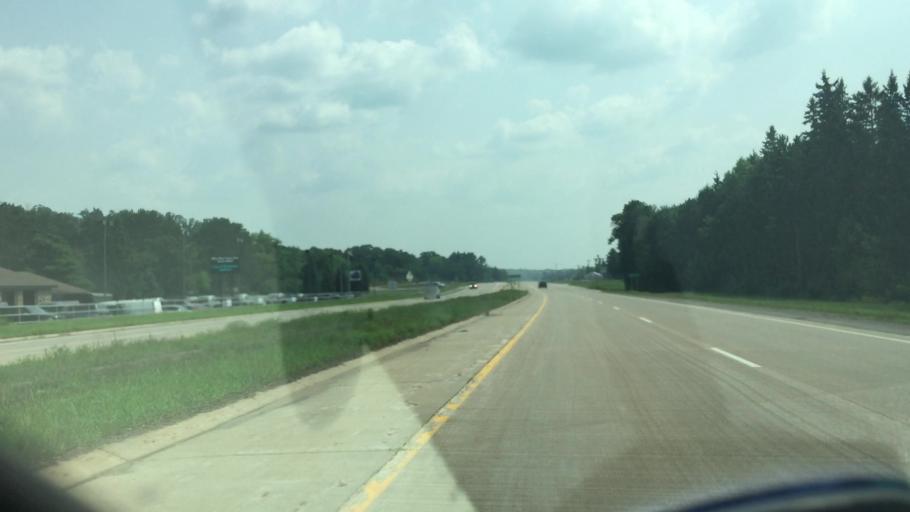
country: US
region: Wisconsin
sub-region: Eau Claire County
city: Altoona
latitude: 44.7546
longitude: -91.4553
